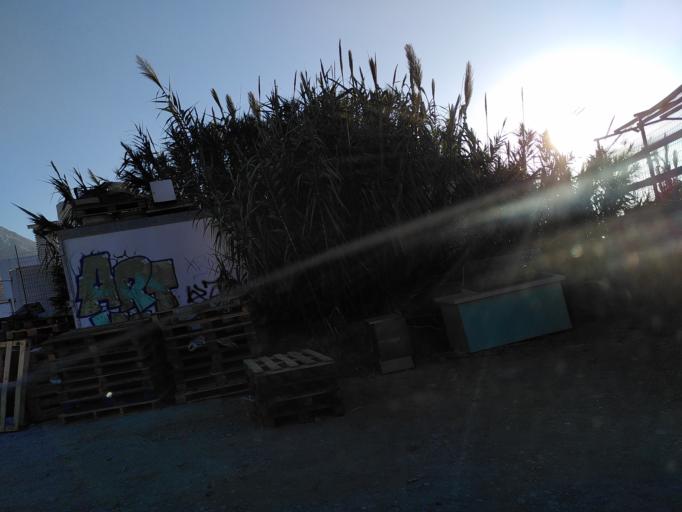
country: GR
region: South Aegean
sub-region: Nomos Kykladon
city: Amorgos
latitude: 36.9040
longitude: 25.9800
